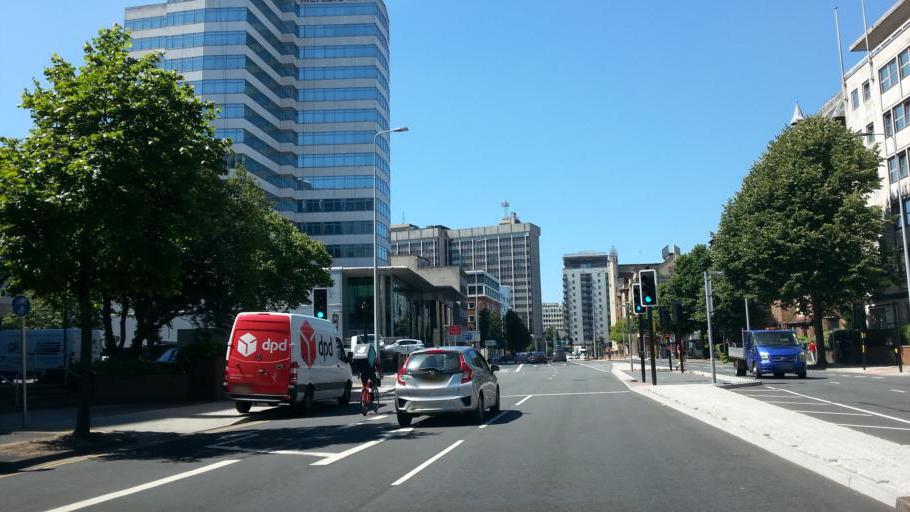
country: GB
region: Wales
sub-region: Cardiff
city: Cardiff
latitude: 51.4845
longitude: -3.1662
